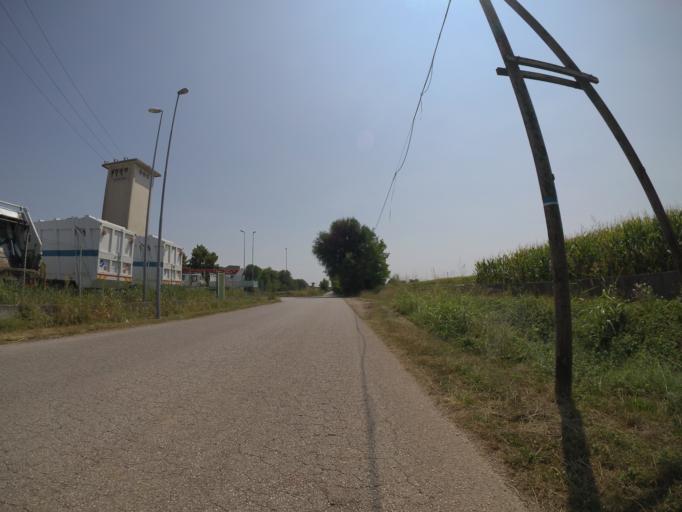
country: IT
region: Friuli Venezia Giulia
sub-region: Provincia di Udine
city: Castions di Strada
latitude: 45.9217
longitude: 13.1751
